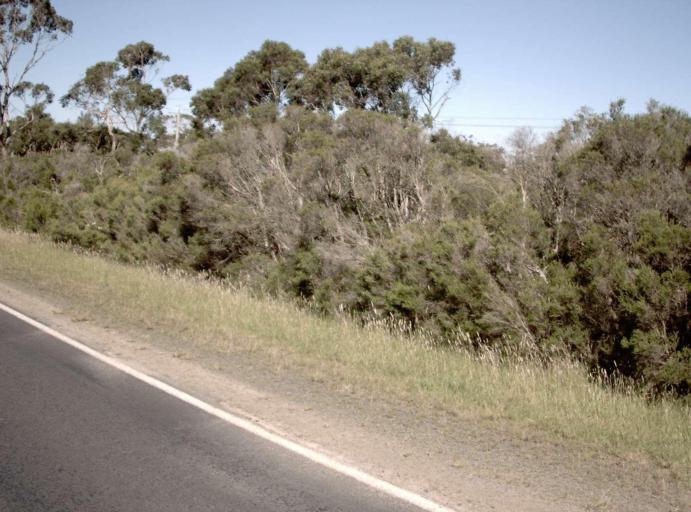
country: AU
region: Victoria
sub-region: Latrobe
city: Morwell
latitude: -38.6382
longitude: 146.5224
